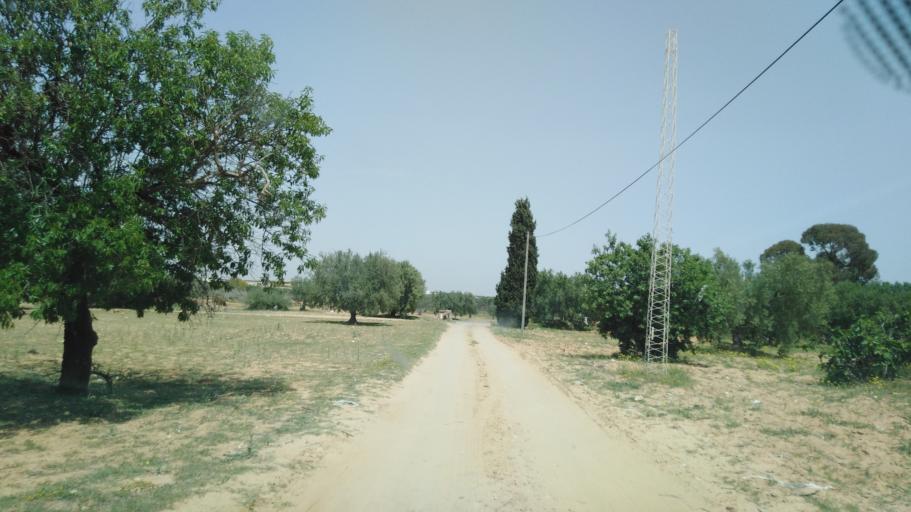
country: TN
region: Safaqis
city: Sfax
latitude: 34.7318
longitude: 10.5551
